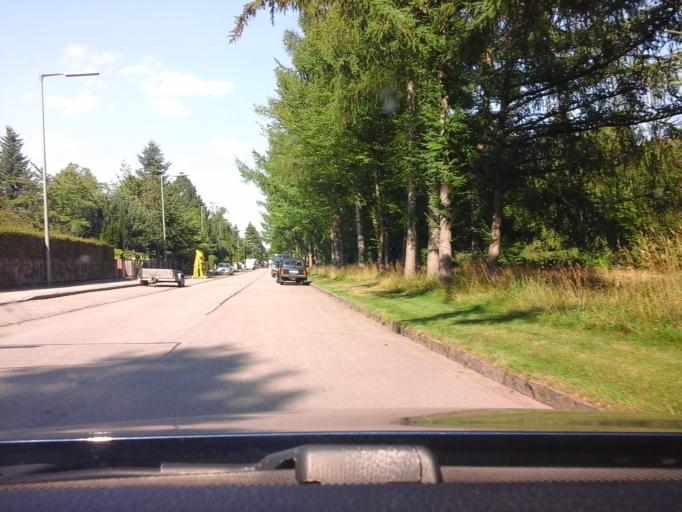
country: DE
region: Bavaria
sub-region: Upper Bavaria
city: Unterhaching
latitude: 48.0917
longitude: 11.5797
